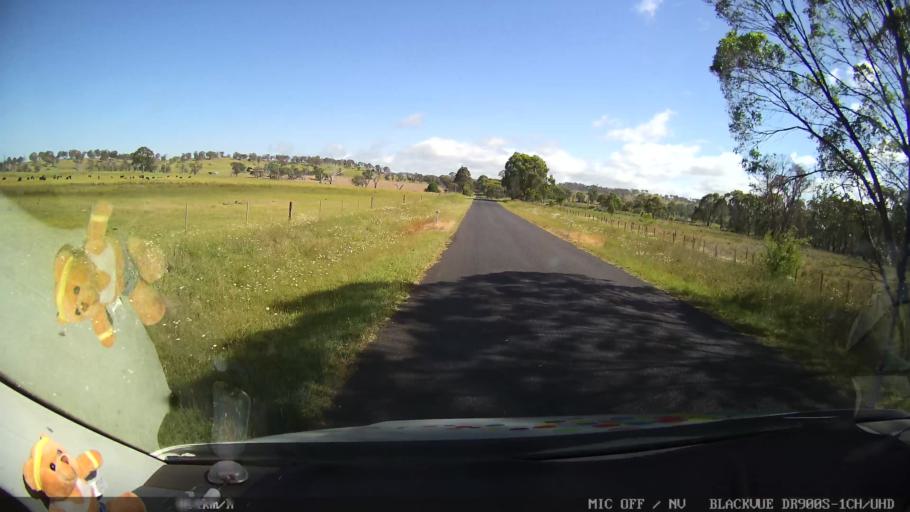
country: AU
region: New South Wales
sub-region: Guyra
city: Guyra
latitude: -30.0996
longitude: 151.6785
